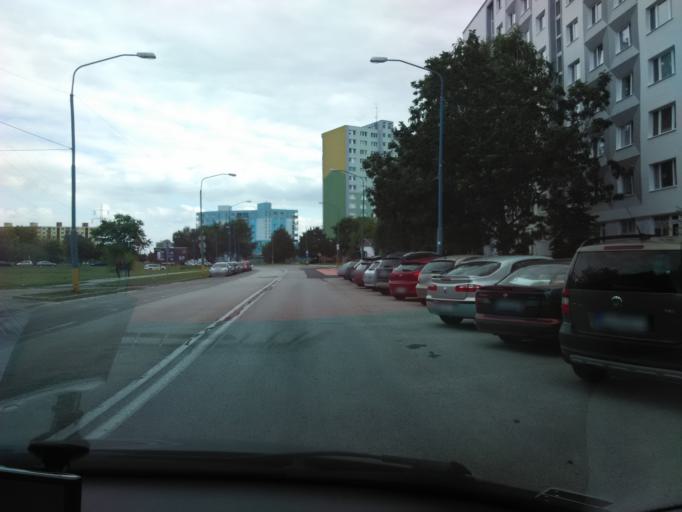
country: SK
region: Bratislavsky
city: Bratislava
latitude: 48.1071
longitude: 17.1033
